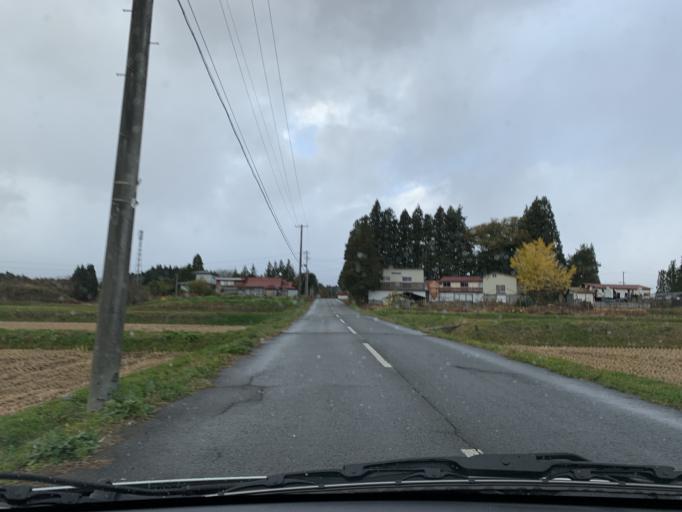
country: JP
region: Iwate
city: Mizusawa
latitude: 39.0942
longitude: 140.9897
